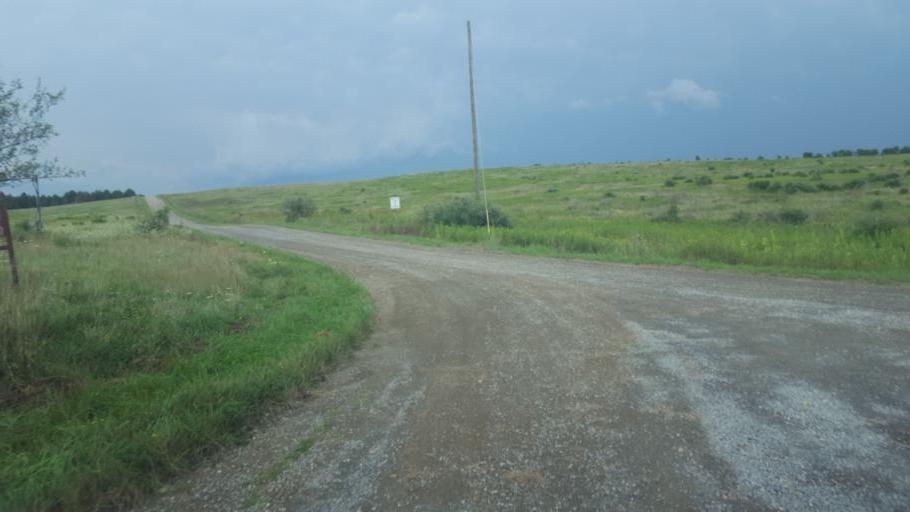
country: US
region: Pennsylvania
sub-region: Clarion County
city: Knox
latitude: 41.1449
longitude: -79.5055
